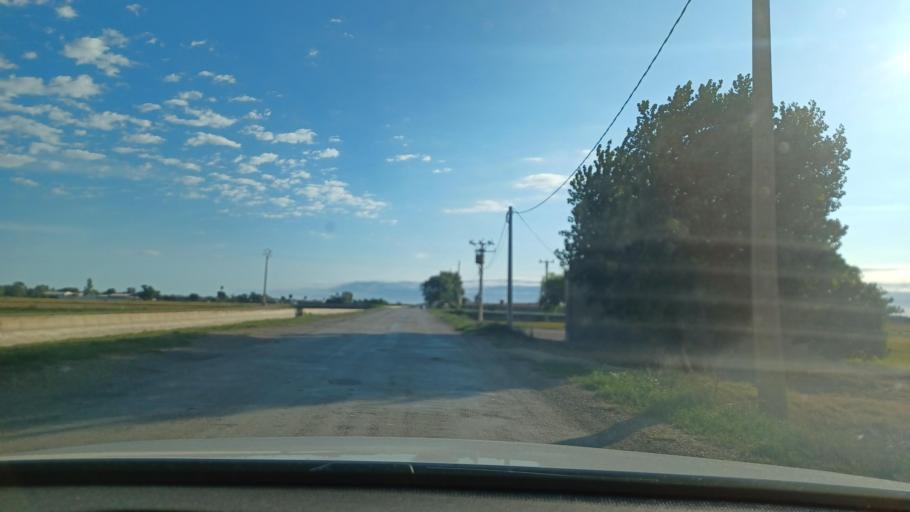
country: ES
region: Catalonia
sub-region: Provincia de Tarragona
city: Amposta
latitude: 40.6994
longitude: 0.6175
